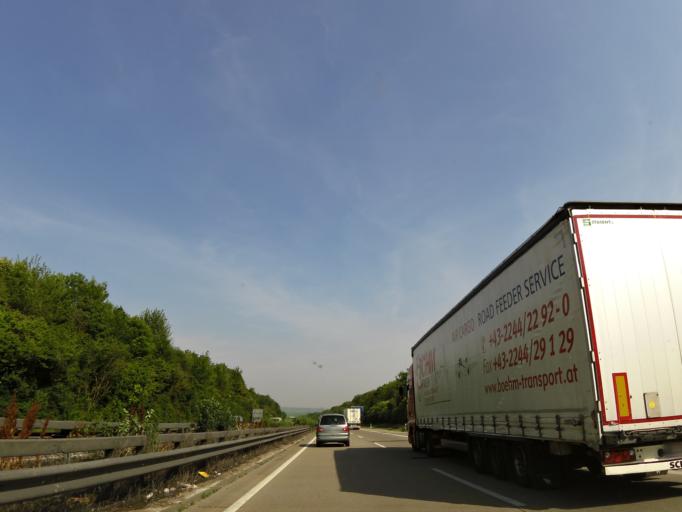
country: DE
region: Rheinland-Pfalz
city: Morstadt
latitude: 49.6562
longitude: 8.2849
